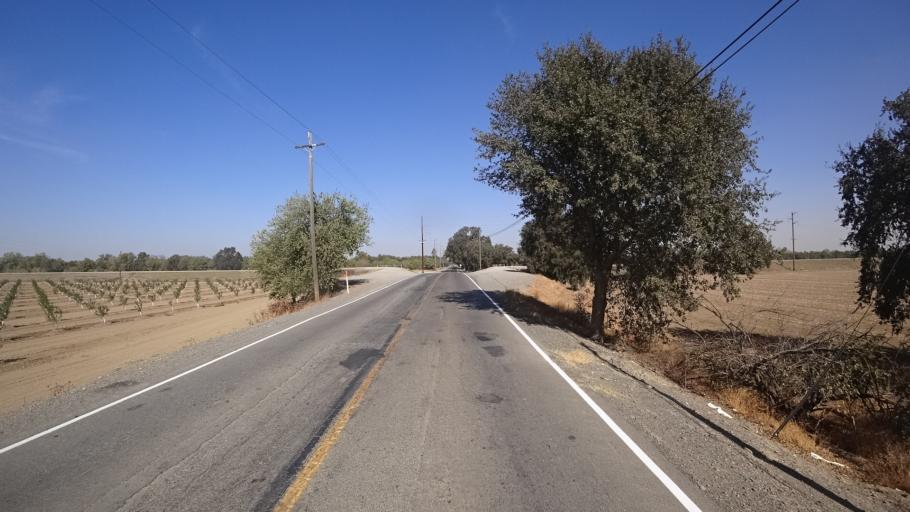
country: US
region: California
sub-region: Yolo County
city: Davis
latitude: 38.5143
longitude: -121.6952
